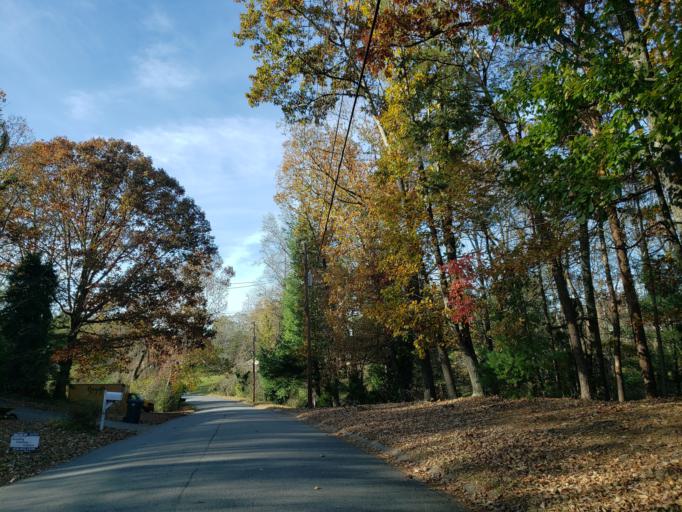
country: US
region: Georgia
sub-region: Cobb County
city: Kennesaw
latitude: 34.0290
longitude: -84.6067
